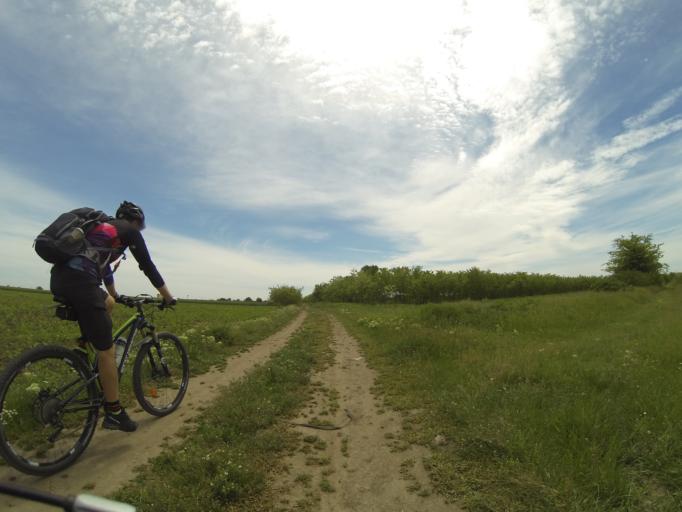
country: RO
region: Dolj
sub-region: Comuna Leu
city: Leu
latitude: 44.2013
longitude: 23.9985
